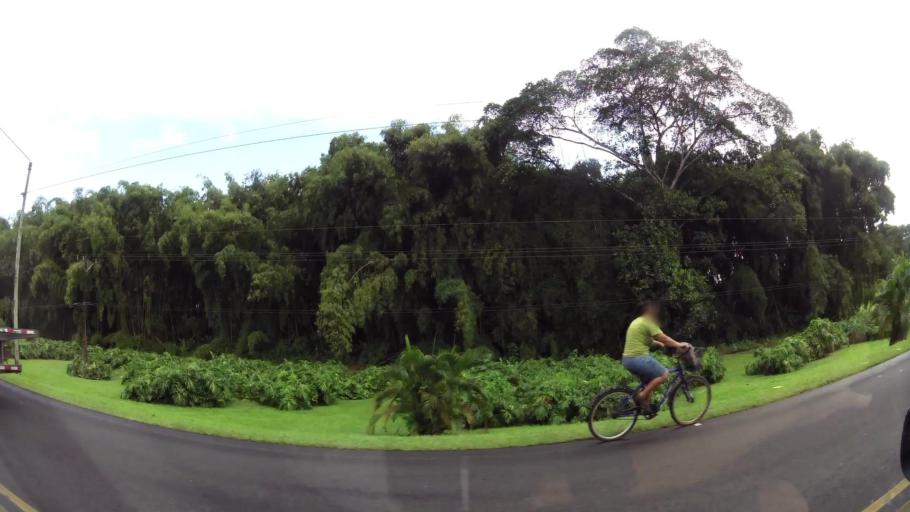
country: CR
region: Limon
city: Pocora
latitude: 10.1749
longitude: -83.6142
